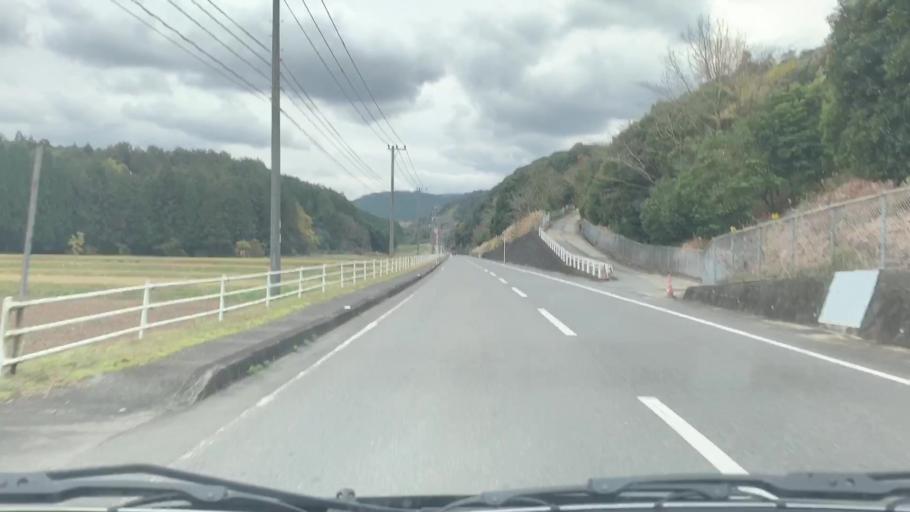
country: JP
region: Saga Prefecture
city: Ureshinomachi-shimojuku
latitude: 33.1209
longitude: 129.9790
